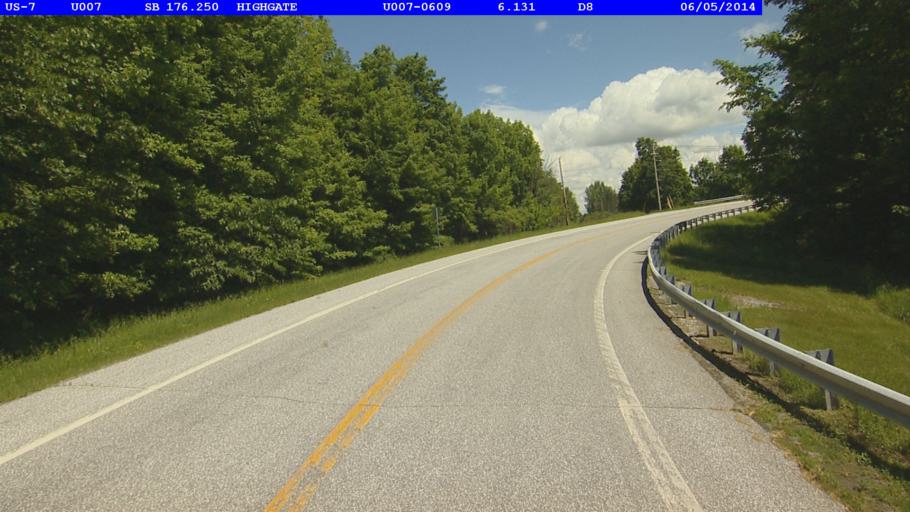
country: US
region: Vermont
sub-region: Franklin County
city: Swanton
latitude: 45.0090
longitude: -73.0881
